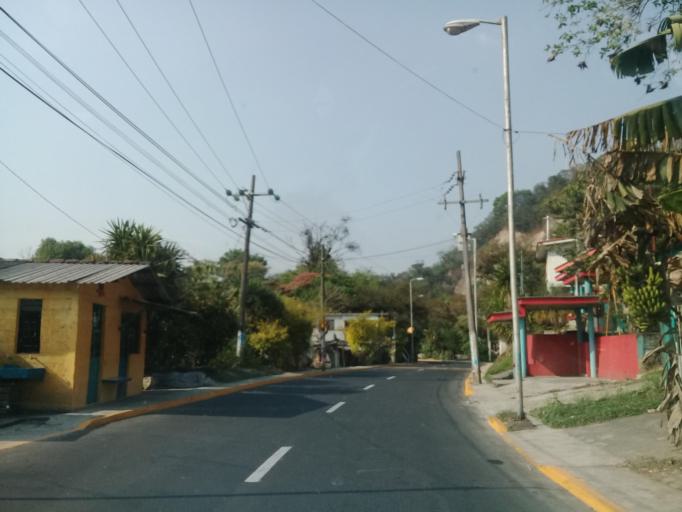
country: MX
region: Veracruz
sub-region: Ixtaczoquitlan
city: Campo Chico
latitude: 18.8489
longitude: -97.0368
